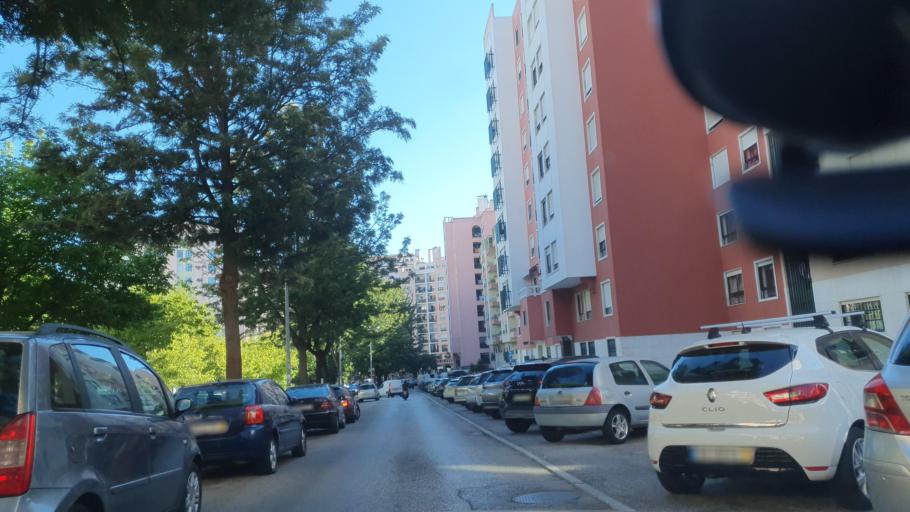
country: PT
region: Lisbon
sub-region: Sintra
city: Cacem
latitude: 38.7553
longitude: -9.2784
